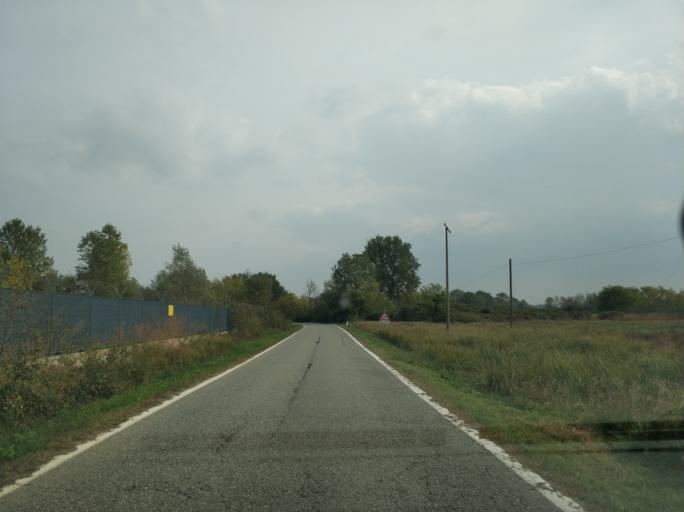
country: IT
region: Piedmont
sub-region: Provincia di Torino
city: San Francesco al Campo
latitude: 45.2426
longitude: 7.6776
